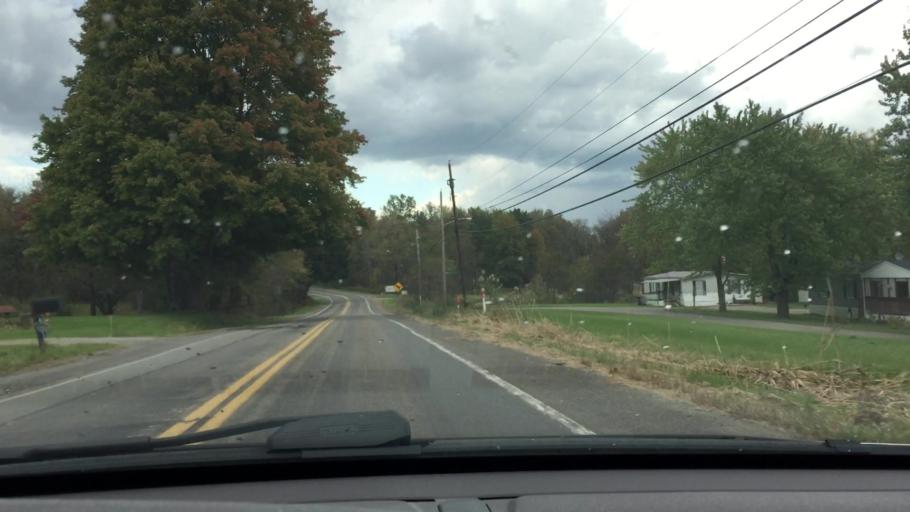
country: US
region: Pennsylvania
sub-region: Lawrence County
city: Oakwood
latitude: 41.0471
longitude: -80.4402
